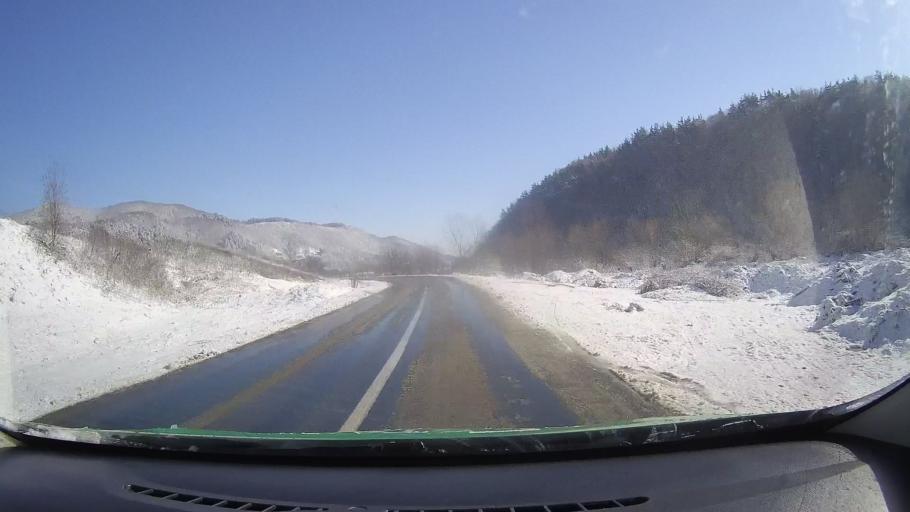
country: RO
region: Sibiu
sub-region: Comuna Talmaciu
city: Talmaciu
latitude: 45.6576
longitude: 24.2741
